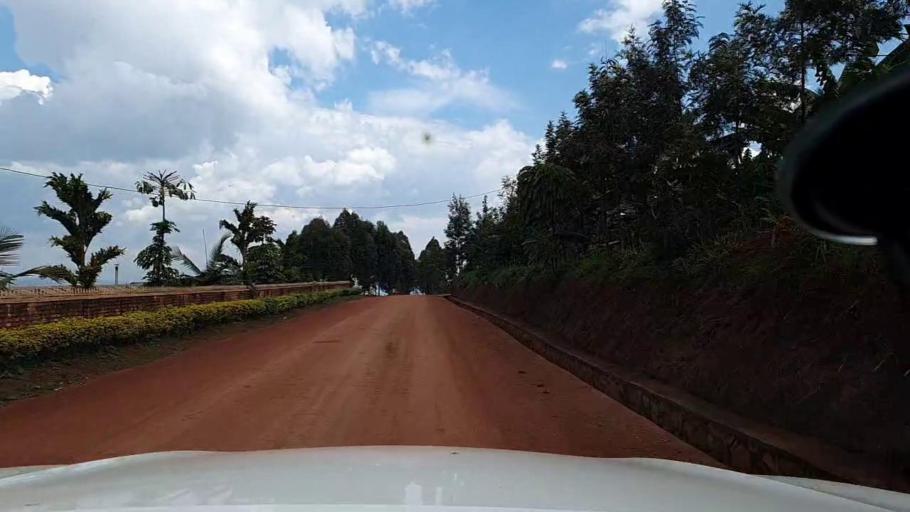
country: RW
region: Kigali
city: Kigali
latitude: -1.8116
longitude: 29.8456
